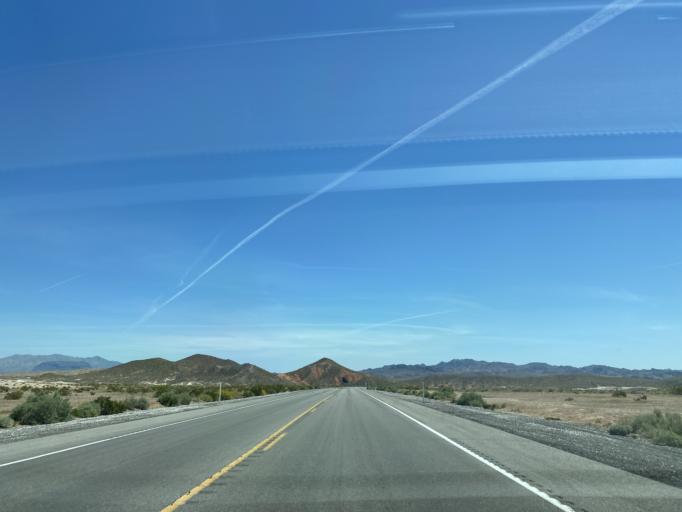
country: US
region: Nevada
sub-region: Clark County
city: Henderson
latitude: 36.1795
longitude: -114.9159
